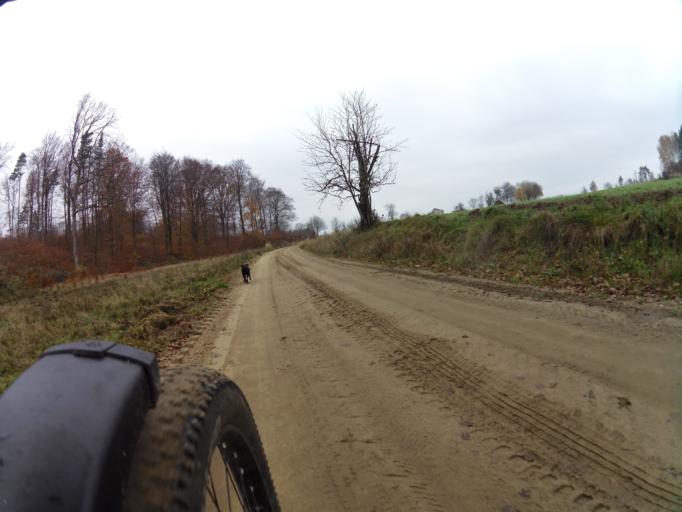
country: PL
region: Pomeranian Voivodeship
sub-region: Powiat pucki
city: Krokowa
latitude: 54.7155
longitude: 18.1392
